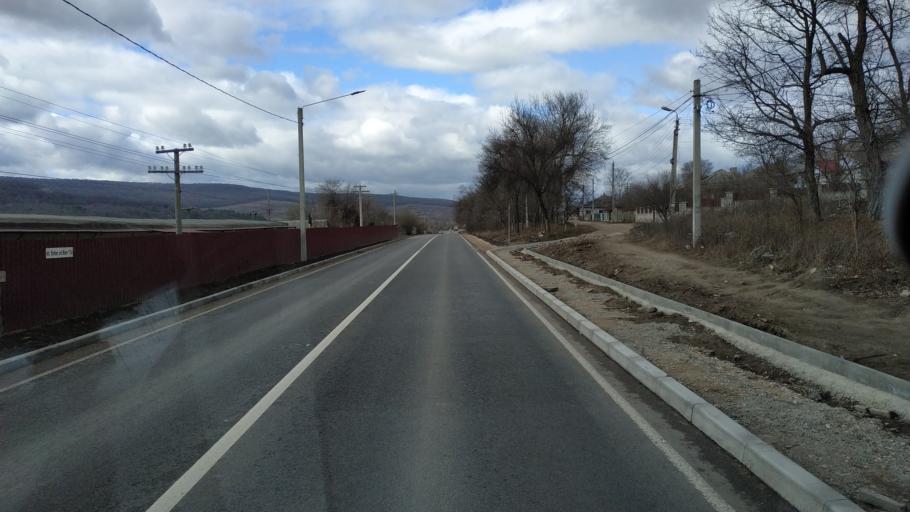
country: MD
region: Stinga Nistrului
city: Bucovat
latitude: 47.1894
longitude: 28.4501
